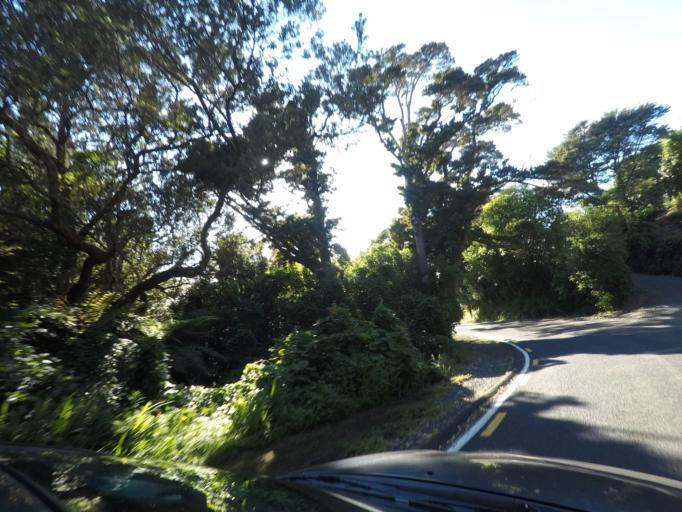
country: NZ
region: Auckland
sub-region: Auckland
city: Titirangi
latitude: -37.0109
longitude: 174.6035
